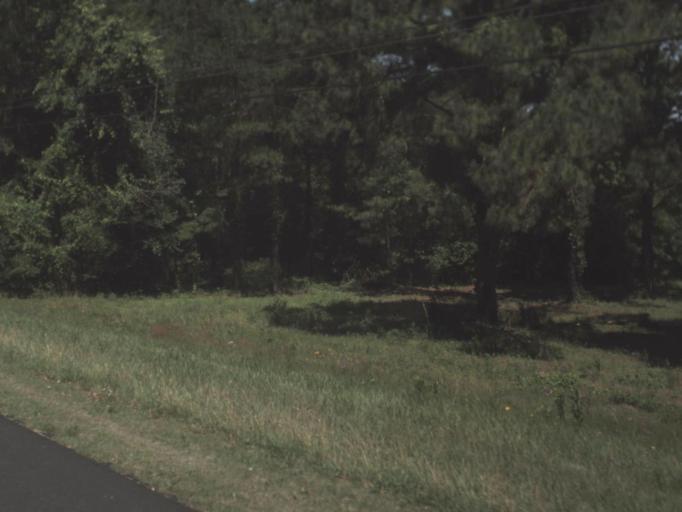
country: US
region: Florida
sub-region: Suwannee County
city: Wellborn
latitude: 30.1921
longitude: -82.7381
